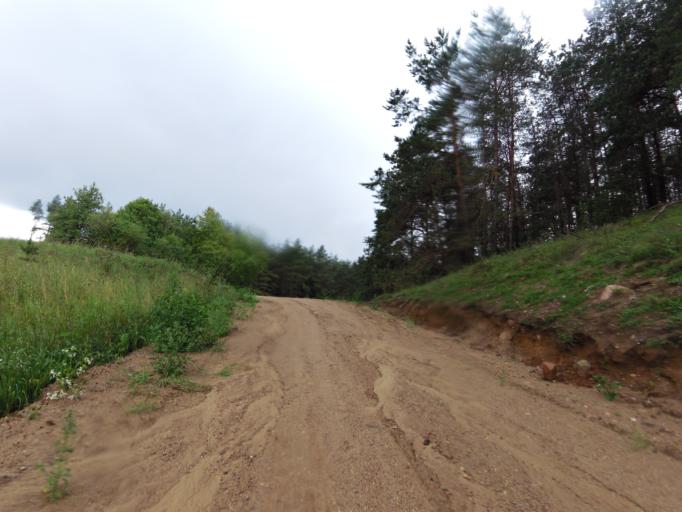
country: LT
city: Grigiskes
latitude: 54.7138
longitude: 25.1117
